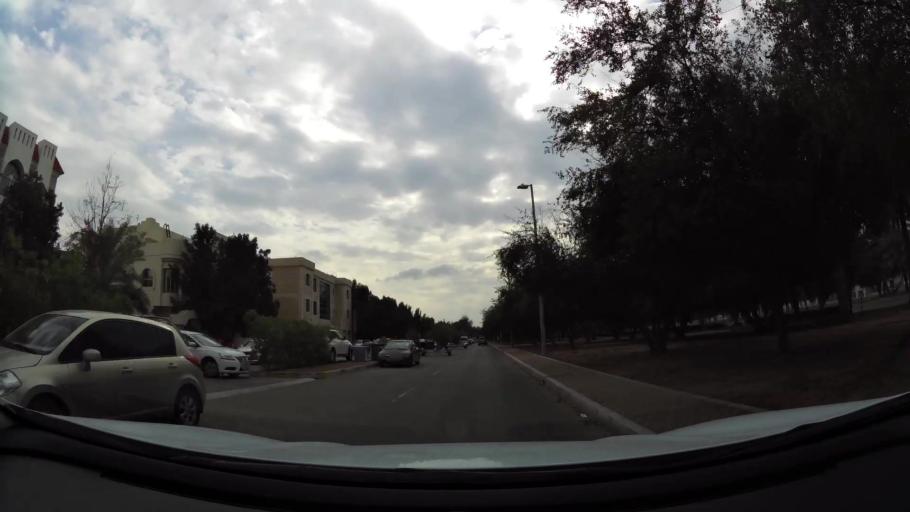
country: AE
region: Abu Dhabi
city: Abu Dhabi
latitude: 24.4457
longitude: 54.3918
